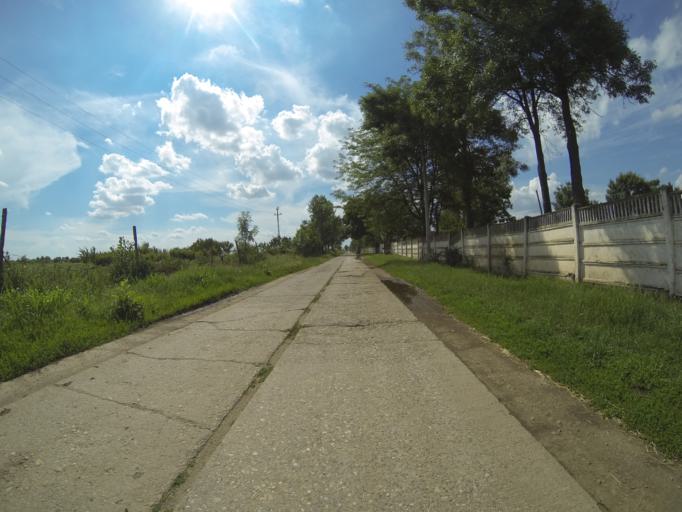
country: RO
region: Dolj
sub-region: Comuna Segarcea
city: Segarcea
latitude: 44.1069
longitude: 23.7406
